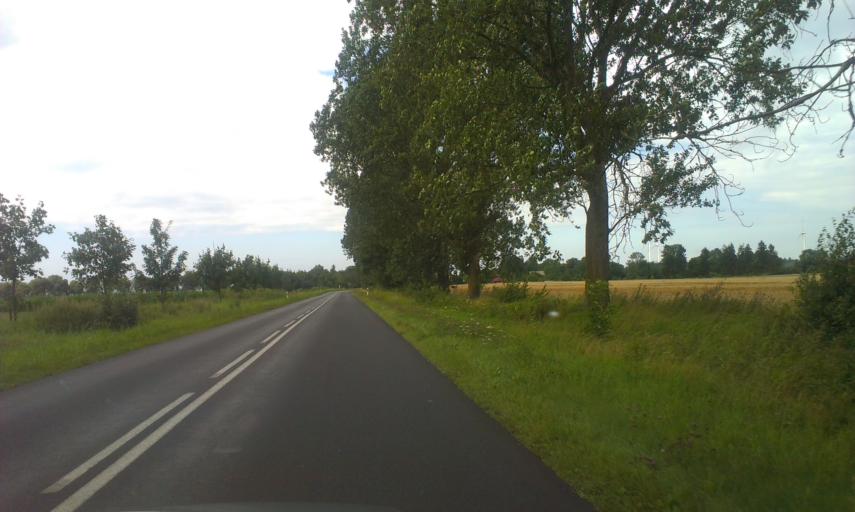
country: PL
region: West Pomeranian Voivodeship
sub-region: Powiat bialogardzki
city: Karlino
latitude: 54.1080
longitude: 15.8214
